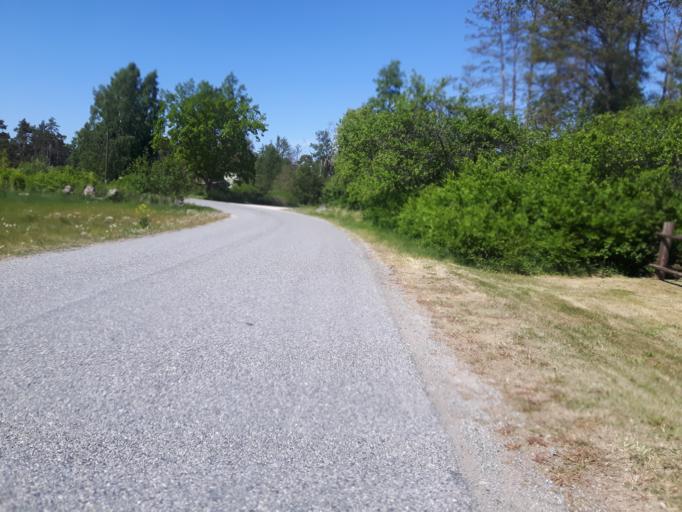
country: EE
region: Laeaene-Virumaa
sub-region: Haljala vald
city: Haljala
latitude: 59.5676
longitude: 26.2994
